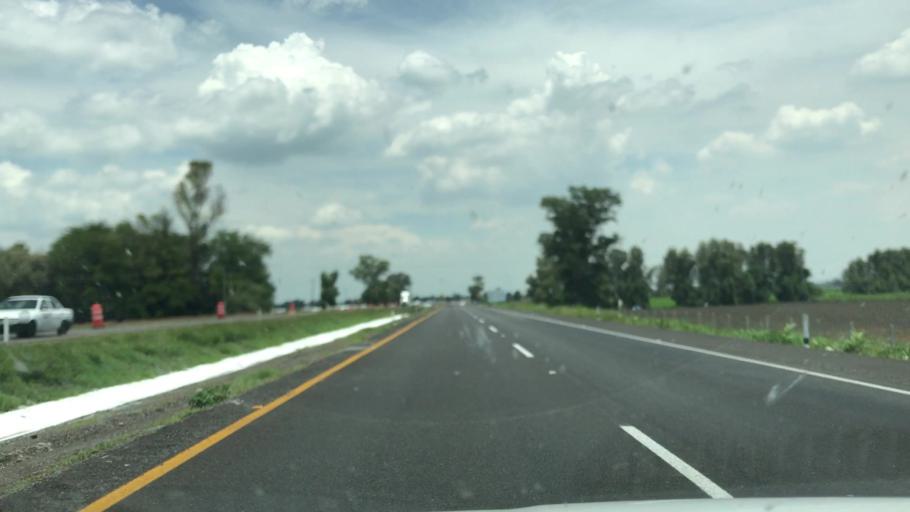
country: MX
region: Guanajuato
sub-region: Irapuato
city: Cuarta Brigada
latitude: 20.6423
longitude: -101.2688
